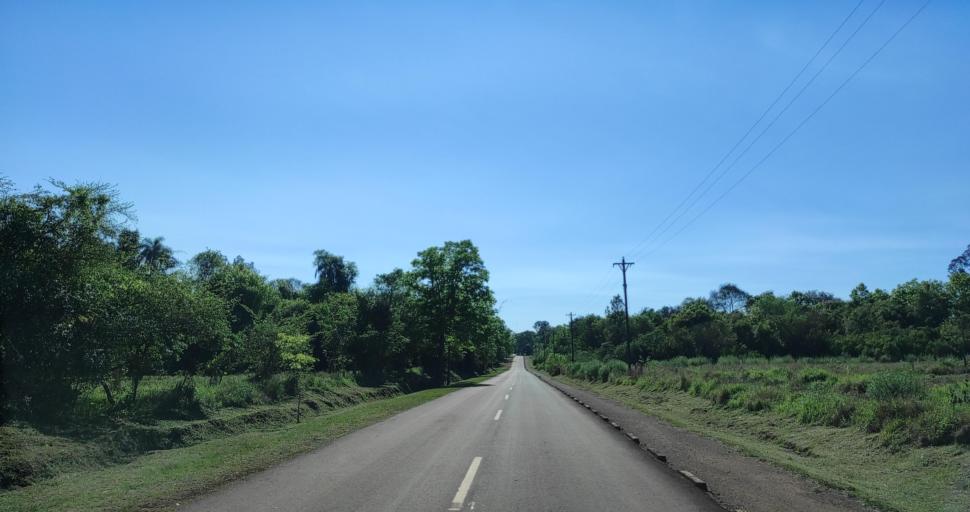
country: AR
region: Misiones
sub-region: Departamento de Candelaria
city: Loreto
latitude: -27.3360
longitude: -55.5266
